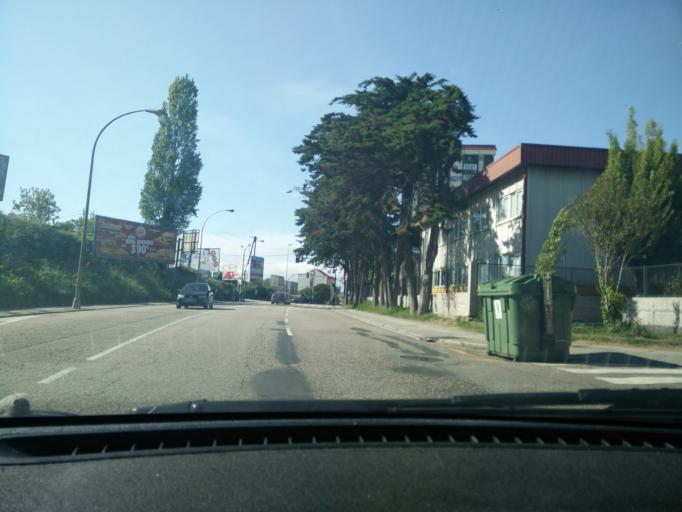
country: ES
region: Galicia
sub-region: Provincia de Pontevedra
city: Vigo
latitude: 42.2162
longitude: -8.7536
